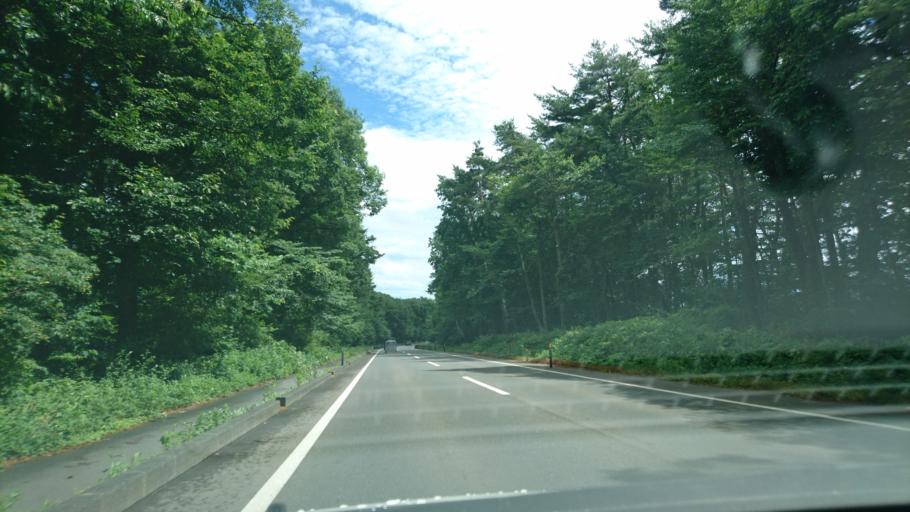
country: JP
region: Iwate
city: Morioka-shi
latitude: 39.7869
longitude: 141.1241
